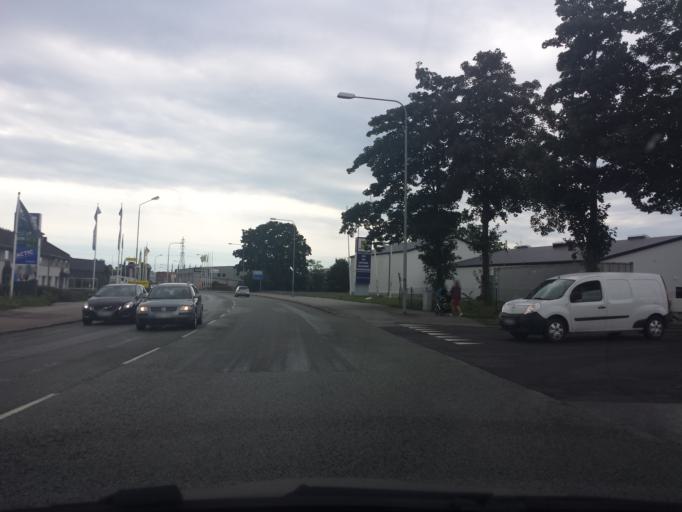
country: SE
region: Skane
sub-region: Ystads Kommun
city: Ystad
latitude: 55.4384
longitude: 13.8354
